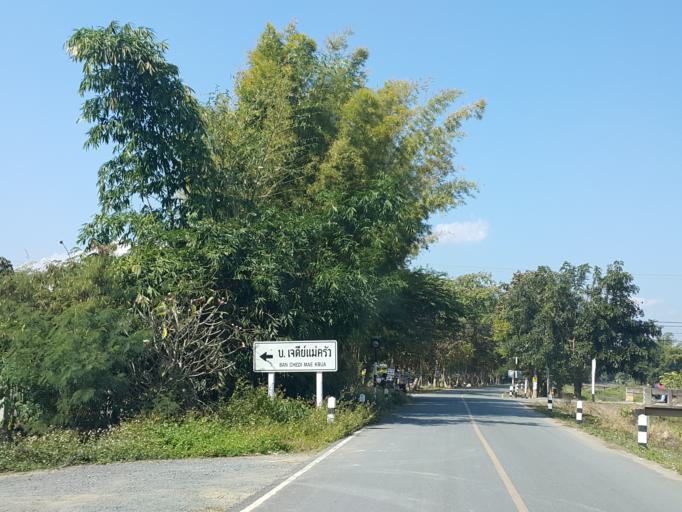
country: TH
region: Chiang Mai
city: Mae Taeng
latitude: 18.9792
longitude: 98.9834
